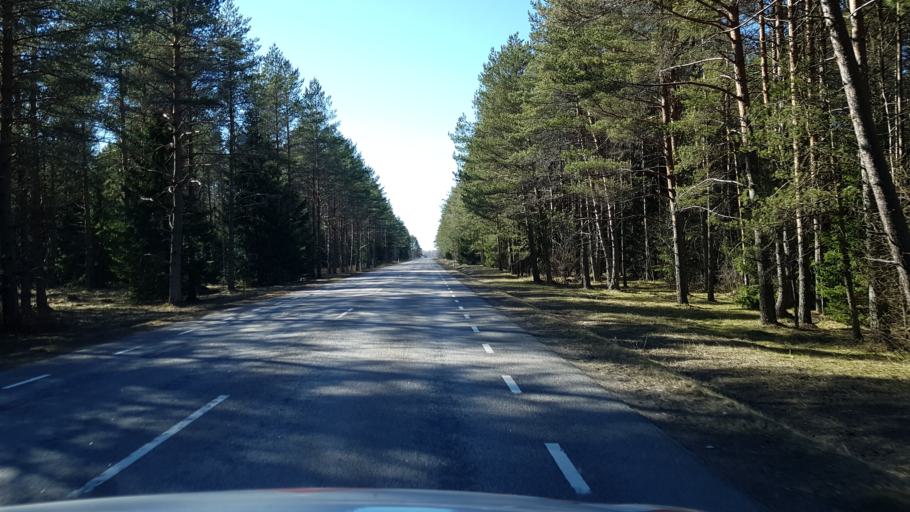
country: EE
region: Laeaene-Virumaa
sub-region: Viru-Nigula vald
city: Kunda
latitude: 59.3590
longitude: 26.6373
